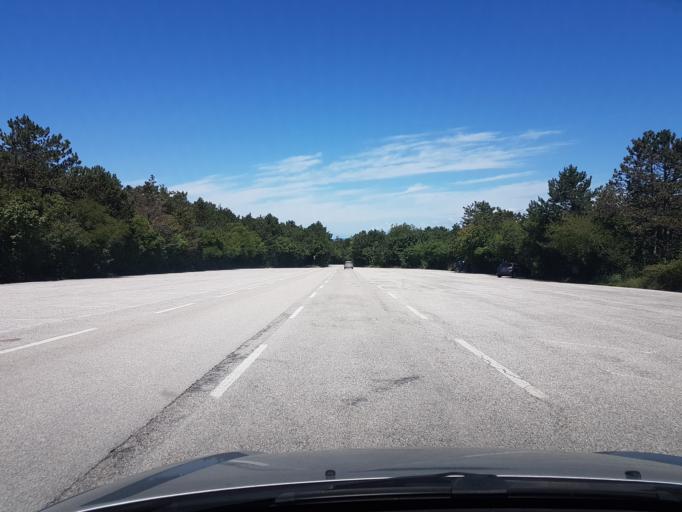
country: IT
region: Friuli Venezia Giulia
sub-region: Provincia di Trieste
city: Prosecco-Contovello
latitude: 45.6968
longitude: 13.7474
